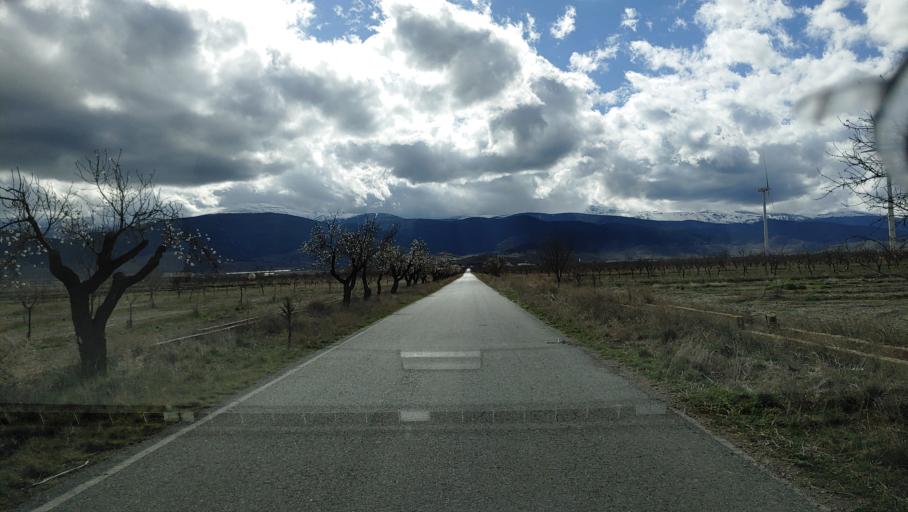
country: ES
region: Andalusia
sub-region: Provincia de Granada
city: Hueneja
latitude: 37.2060
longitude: -2.9773
